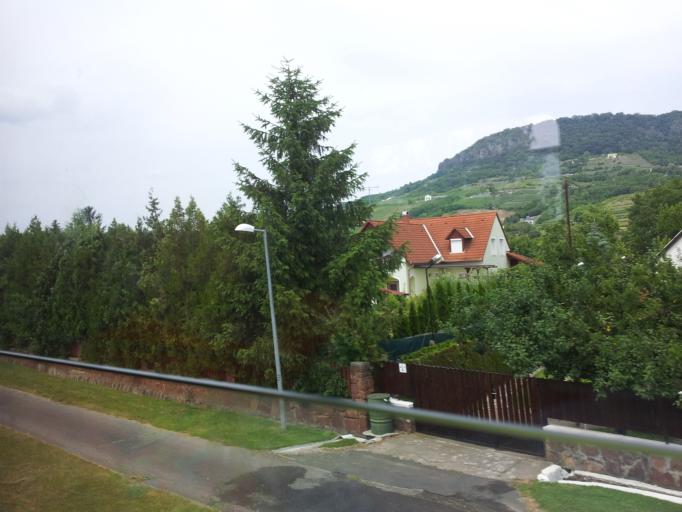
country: HU
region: Veszprem
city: Badacsonytomaj
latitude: 46.7850
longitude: 17.4960
